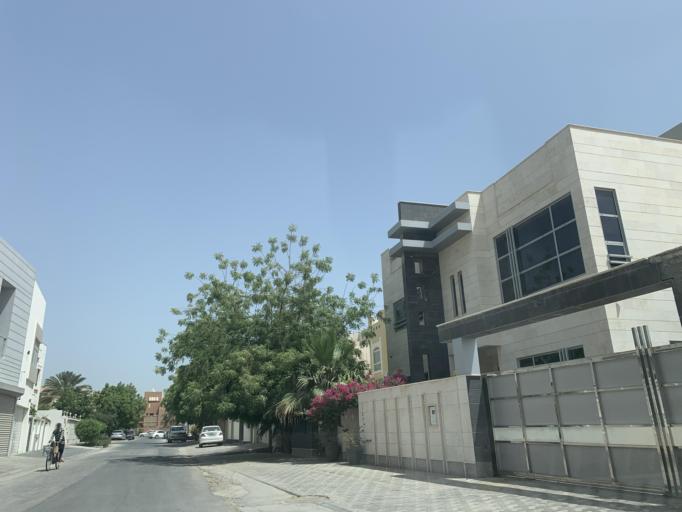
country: BH
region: Northern
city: Ar Rifa'
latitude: 26.1546
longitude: 50.5826
